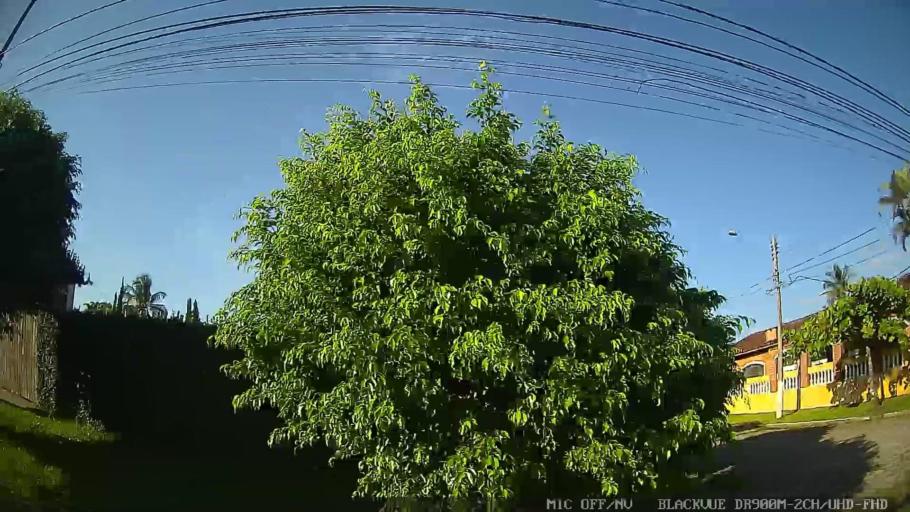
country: BR
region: Sao Paulo
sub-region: Peruibe
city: Peruibe
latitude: -24.2861
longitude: -46.9628
